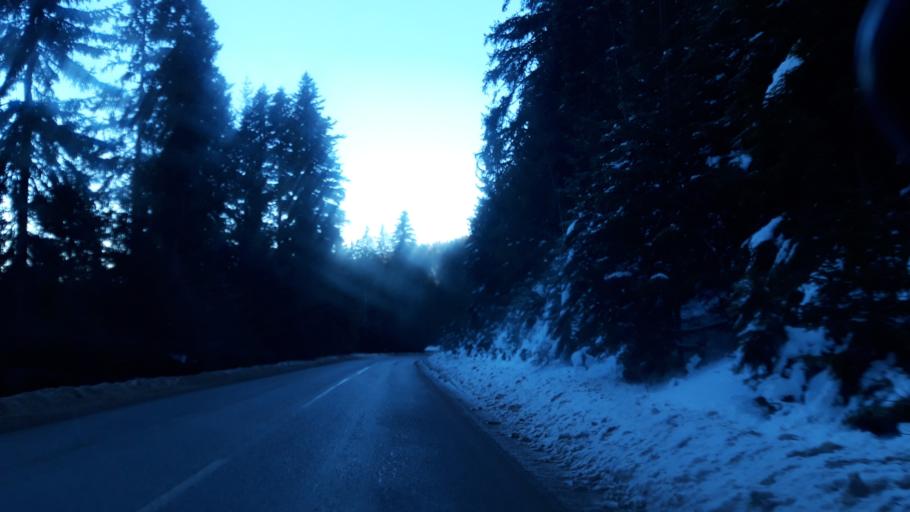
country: BA
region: Republika Srpska
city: Koran
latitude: 43.7717
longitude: 18.5490
